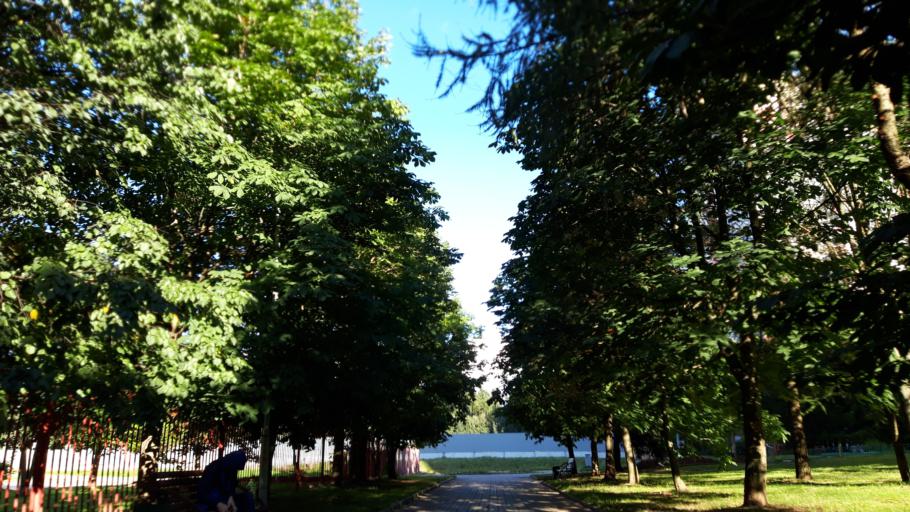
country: RU
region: Moscow
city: Zelenograd
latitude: 55.9870
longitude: 37.1891
